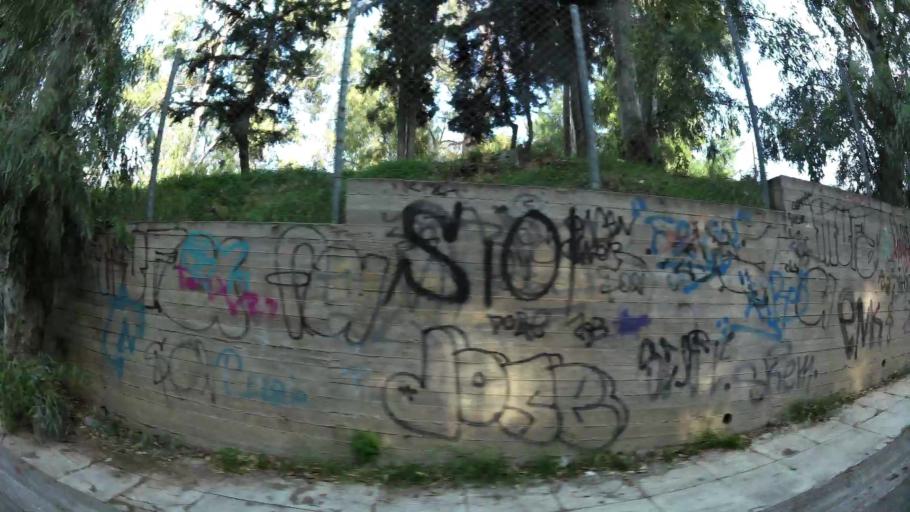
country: GR
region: Attica
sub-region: Nomarchia Athinas
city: Agia Paraskevi
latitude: 38.0079
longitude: 23.8326
